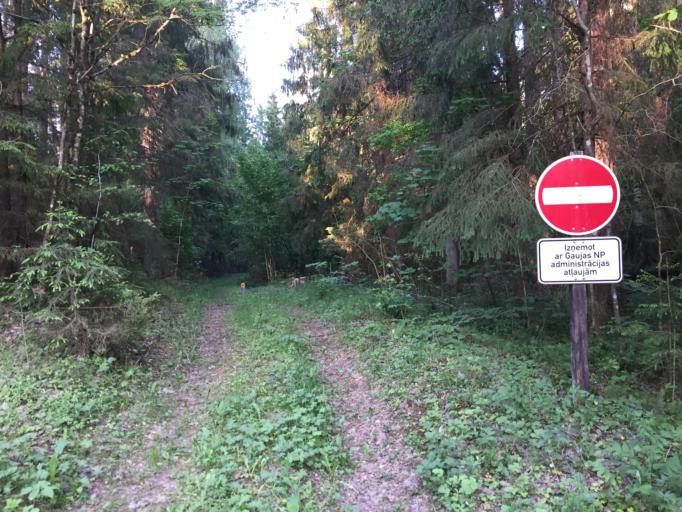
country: LV
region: Ligatne
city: Ligatne
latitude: 57.2598
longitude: 25.0901
